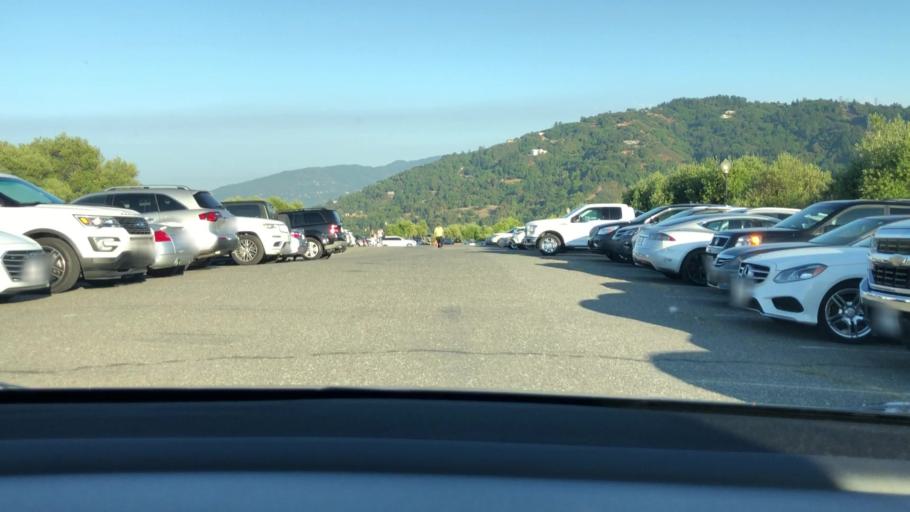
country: US
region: California
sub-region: Santa Clara County
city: Saratoga
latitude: 37.2579
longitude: -122.0640
